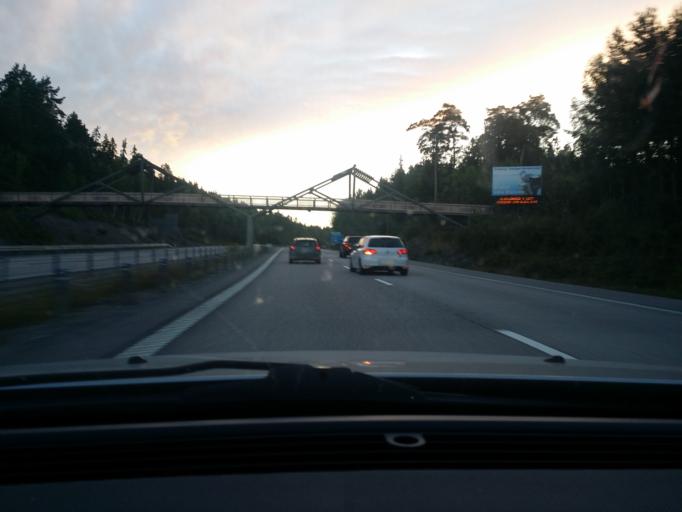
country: SE
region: Uppsala
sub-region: Enkopings Kommun
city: Enkoping
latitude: 59.6493
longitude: 17.0623
